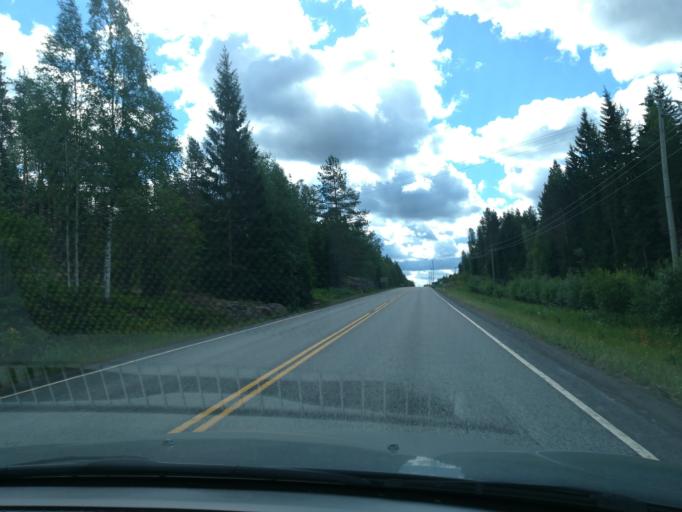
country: FI
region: Southern Savonia
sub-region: Mikkeli
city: Ristiina
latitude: 61.4569
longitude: 27.2596
